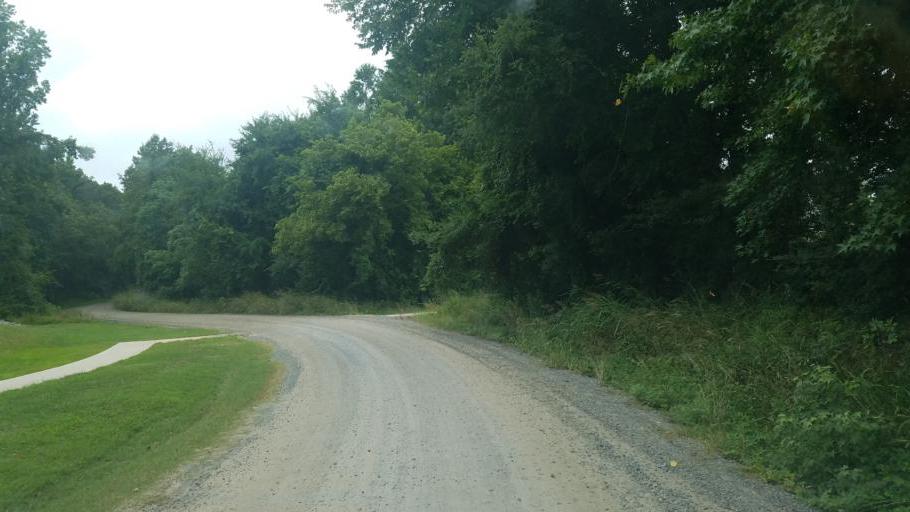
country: US
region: South Carolina
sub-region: York County
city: Fort Mill
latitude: 34.9748
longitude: -80.9680
